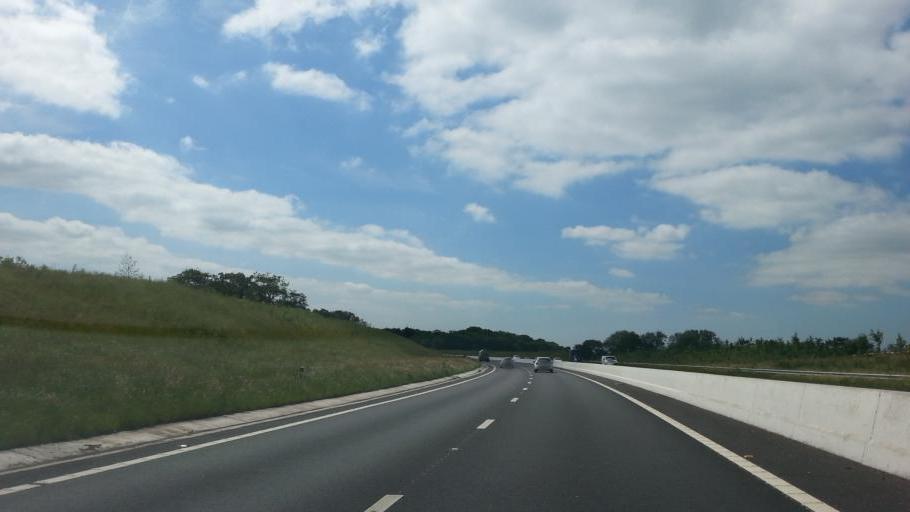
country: GB
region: England
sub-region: Cheshire East
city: Mere
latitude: 53.3323
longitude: -2.4212
